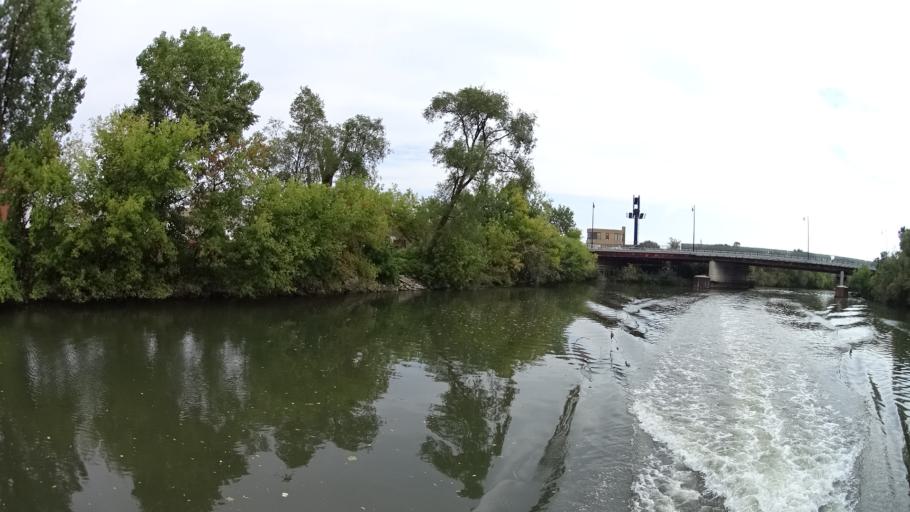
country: US
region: Illinois
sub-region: Cook County
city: Lincolnwood
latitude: 41.9366
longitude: -87.6893
